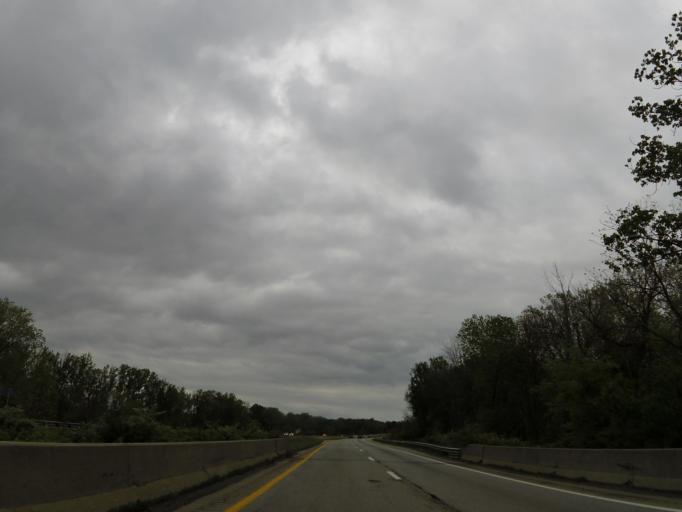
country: US
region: Ohio
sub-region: Franklin County
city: Grove City
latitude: 39.8211
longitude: -83.1691
